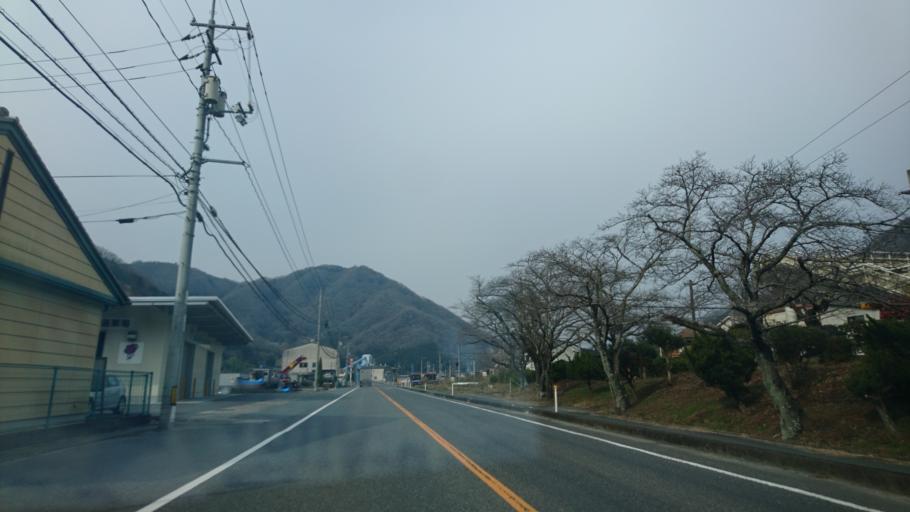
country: JP
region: Okayama
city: Takahashi
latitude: 34.8253
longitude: 133.6148
